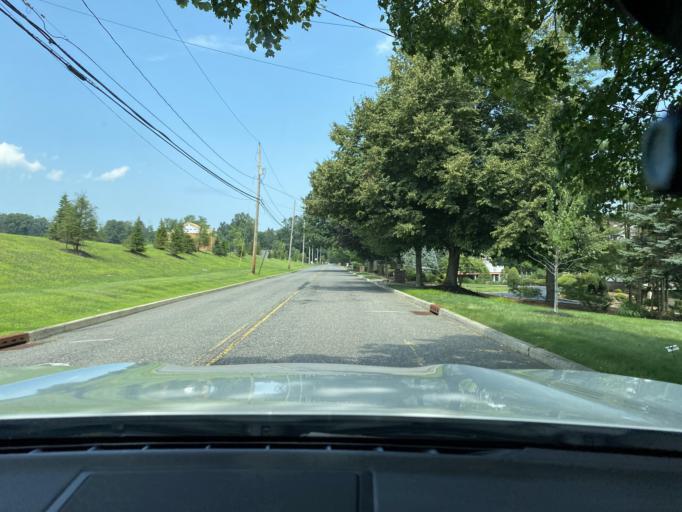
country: US
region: New Jersey
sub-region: Bergen County
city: Upper Saddle River
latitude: 41.0767
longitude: -74.1114
